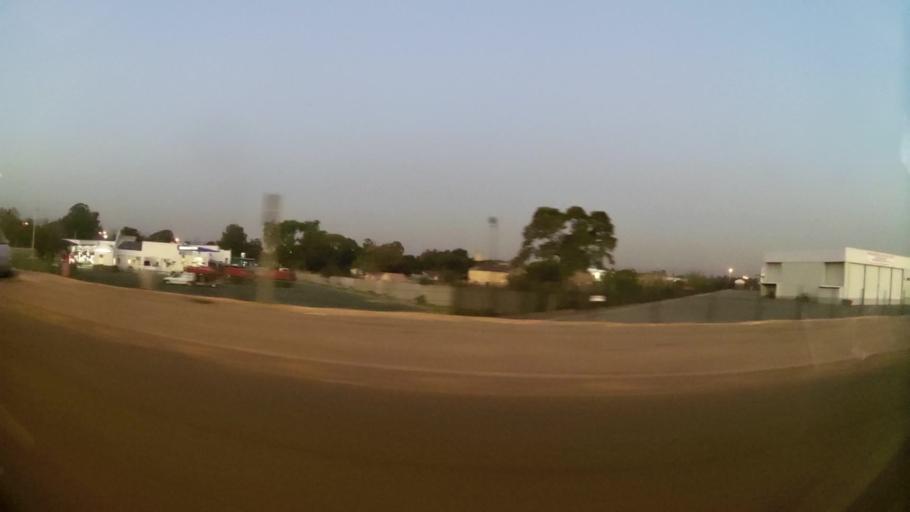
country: ZA
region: North-West
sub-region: Bojanala Platinum District Municipality
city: Rustenburg
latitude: -25.6835
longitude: 27.2551
